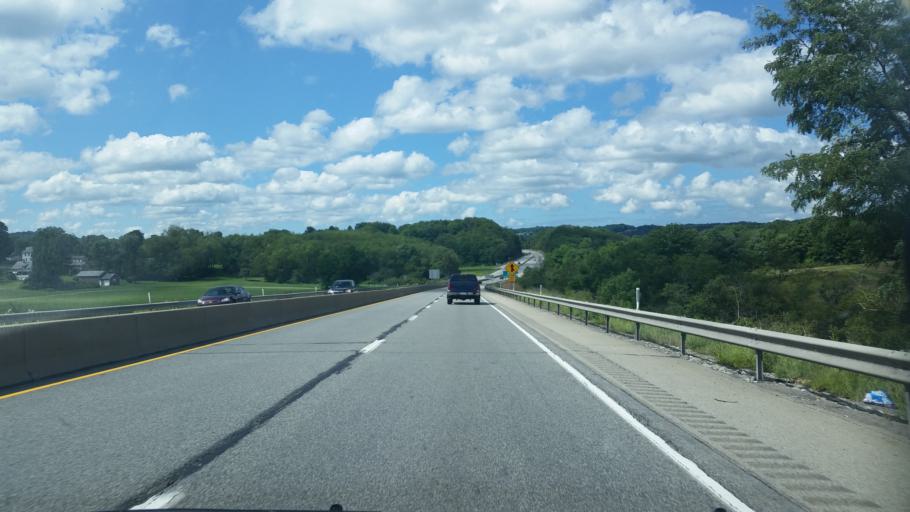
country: US
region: Pennsylvania
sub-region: Cambria County
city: Westmont
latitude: 40.4568
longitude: -79.0244
